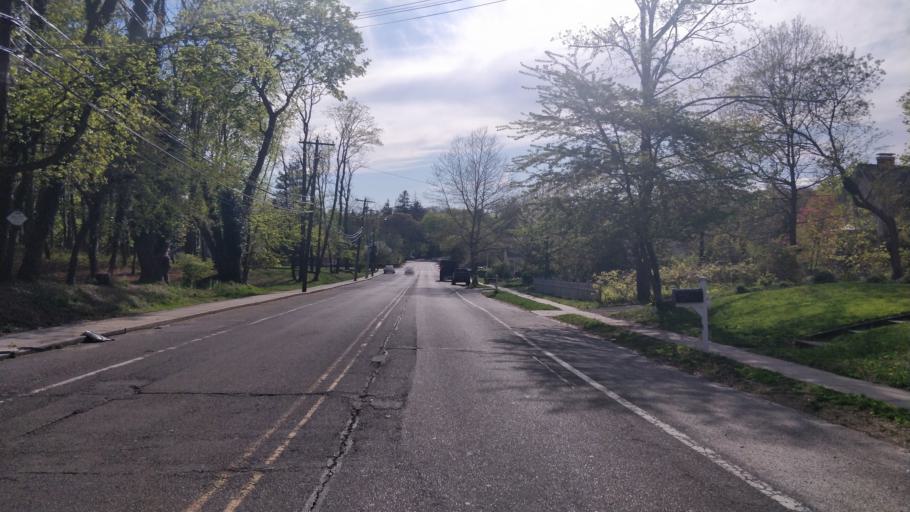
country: US
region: New York
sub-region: Suffolk County
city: East Setauket
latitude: 40.9454
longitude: -73.1133
